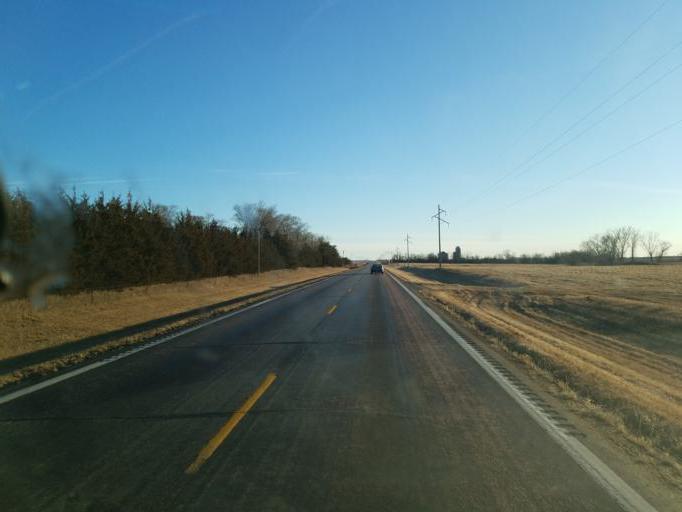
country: US
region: South Dakota
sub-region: Bon Homme County
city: Tyndall
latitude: 42.9483
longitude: -97.8919
